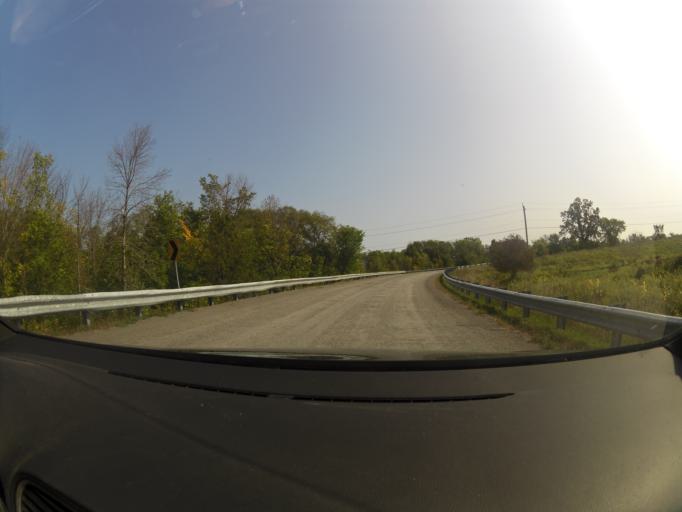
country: CA
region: Ontario
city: Carleton Place
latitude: 45.3234
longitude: -76.0994
